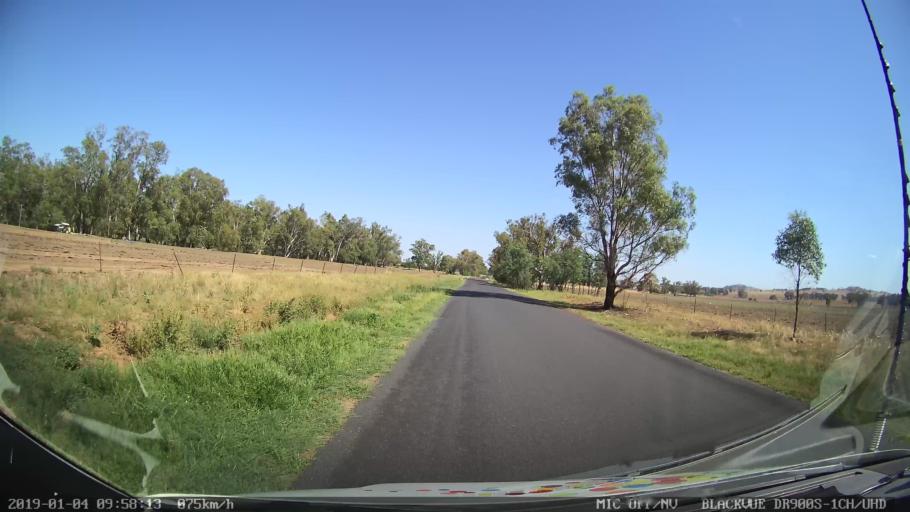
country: AU
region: New South Wales
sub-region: Cabonne
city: Canowindra
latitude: -33.5205
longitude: 148.3960
